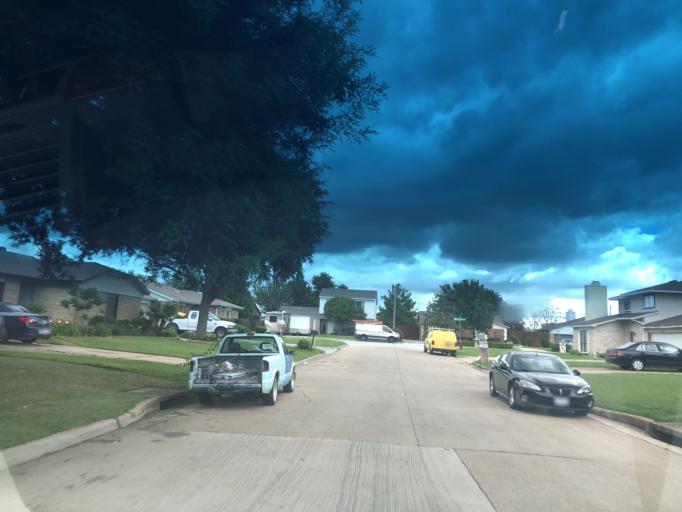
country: US
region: Texas
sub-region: Dallas County
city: Grand Prairie
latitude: 32.6976
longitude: -97.0103
